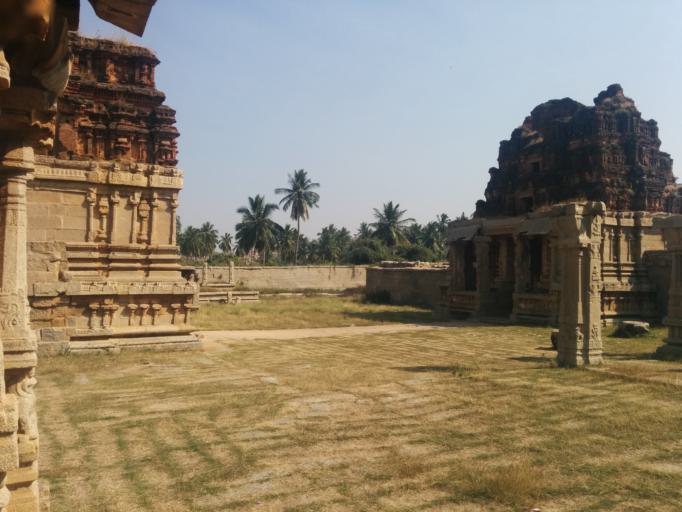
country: IN
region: Karnataka
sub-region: Bellary
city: Hampi
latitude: 15.3326
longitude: 76.4698
